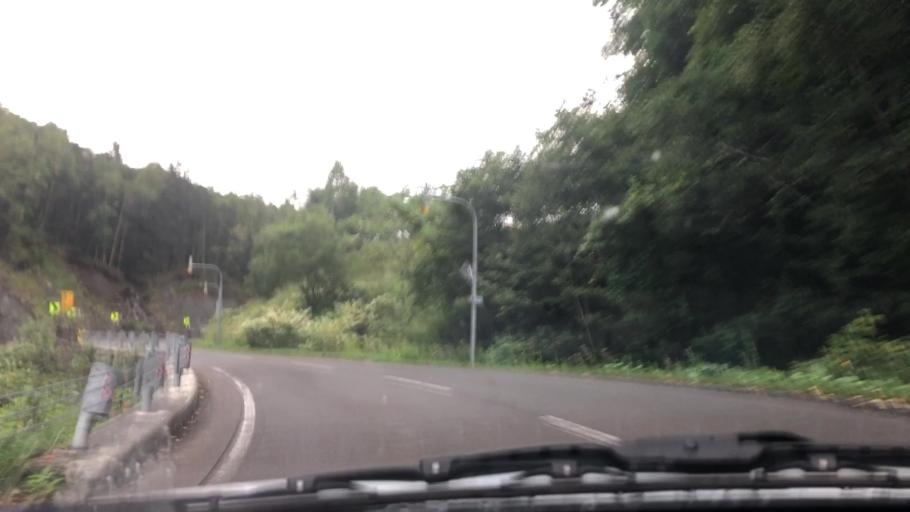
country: JP
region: Hokkaido
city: Shimo-furano
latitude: 42.9370
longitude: 142.3734
